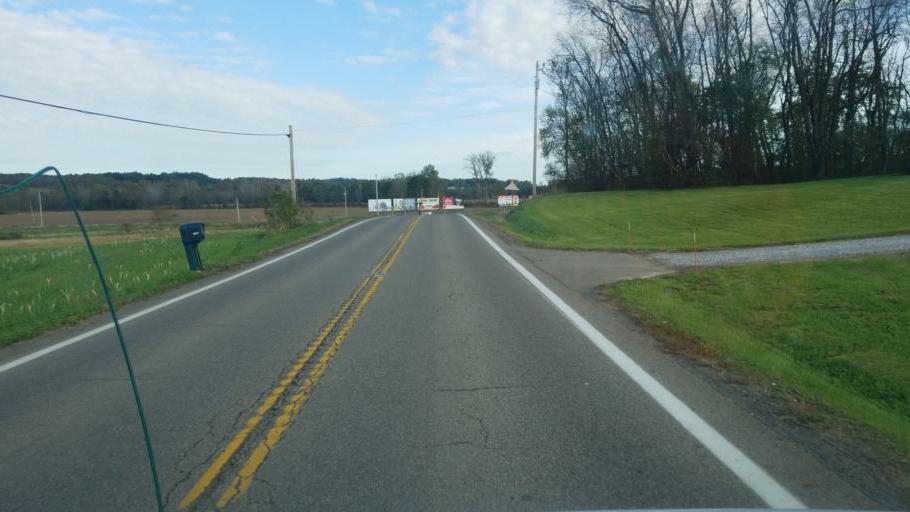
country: US
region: Ohio
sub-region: Holmes County
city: Millersburg
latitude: 40.6372
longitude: -81.9264
